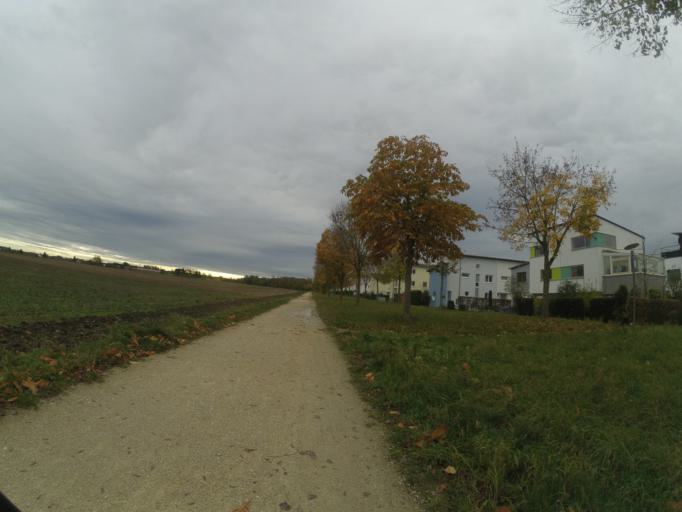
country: DE
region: Bavaria
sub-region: Swabia
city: Neu-Ulm
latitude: 48.3793
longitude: 10.0145
